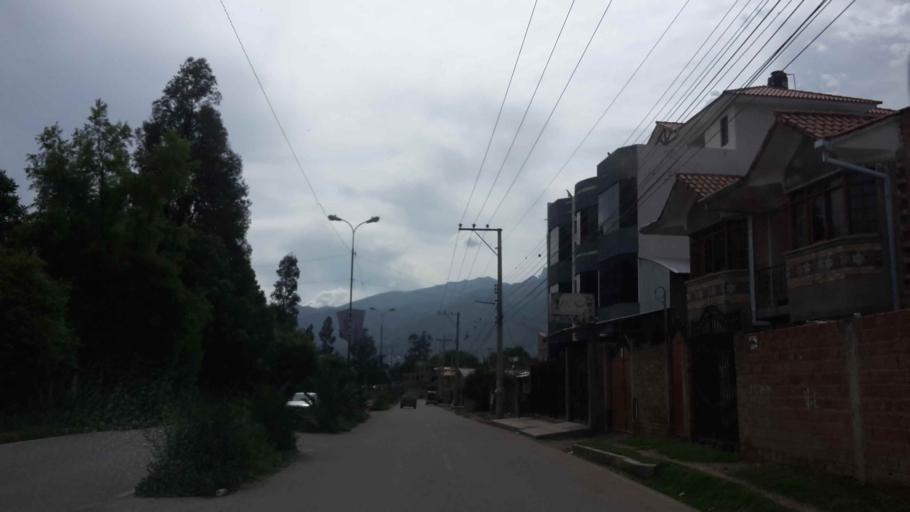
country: BO
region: Cochabamba
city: Cochabamba
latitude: -17.3290
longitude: -66.2444
